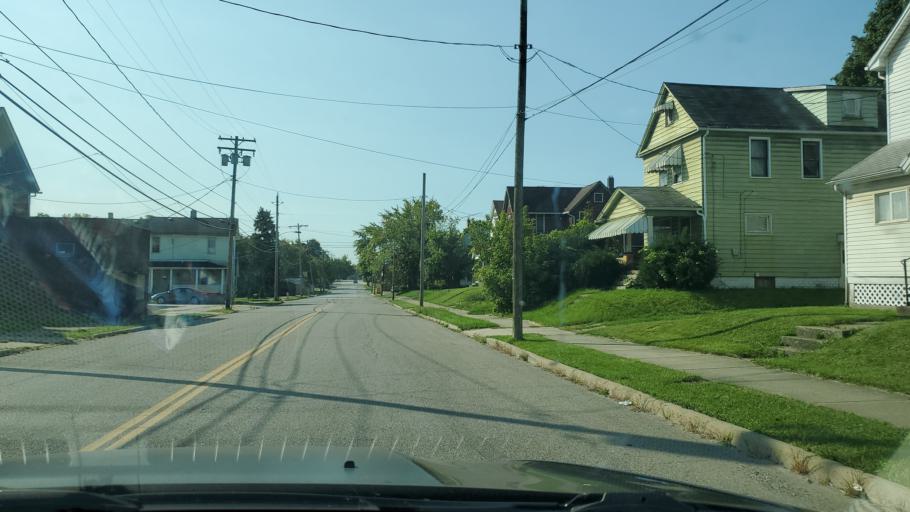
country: US
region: Ohio
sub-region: Mahoning County
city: Youngstown
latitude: 41.1084
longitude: -80.6829
